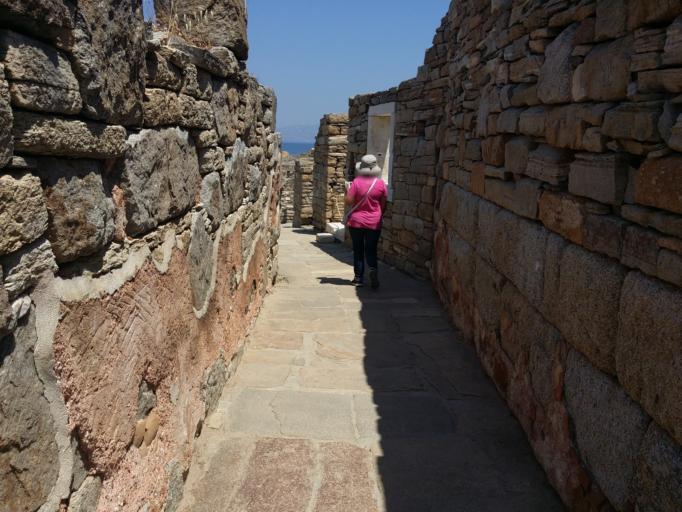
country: GR
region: South Aegean
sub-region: Nomos Kykladon
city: Mykonos
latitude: 37.3973
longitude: 25.2675
